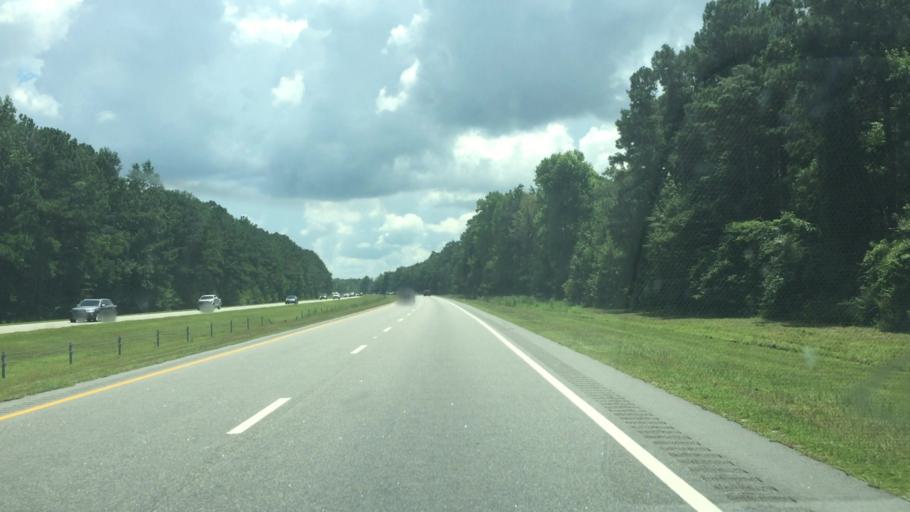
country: US
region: North Carolina
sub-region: Columbus County
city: Chadbourn
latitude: 34.4080
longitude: -78.9268
